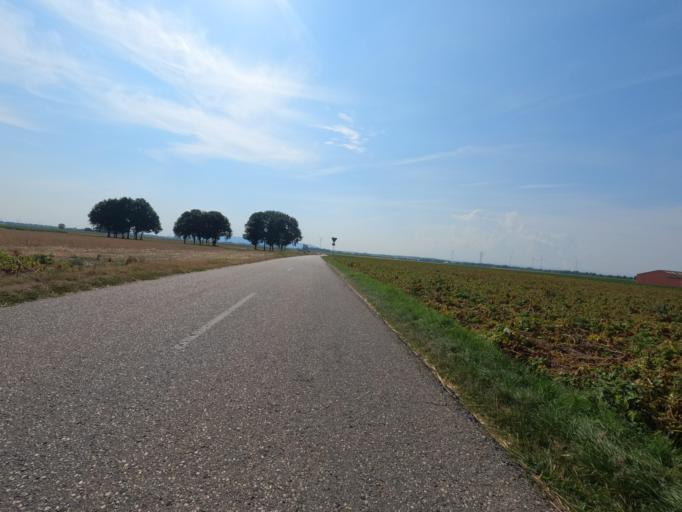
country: DE
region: North Rhine-Westphalia
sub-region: Regierungsbezirk Koln
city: Titz
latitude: 50.9988
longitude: 6.3489
